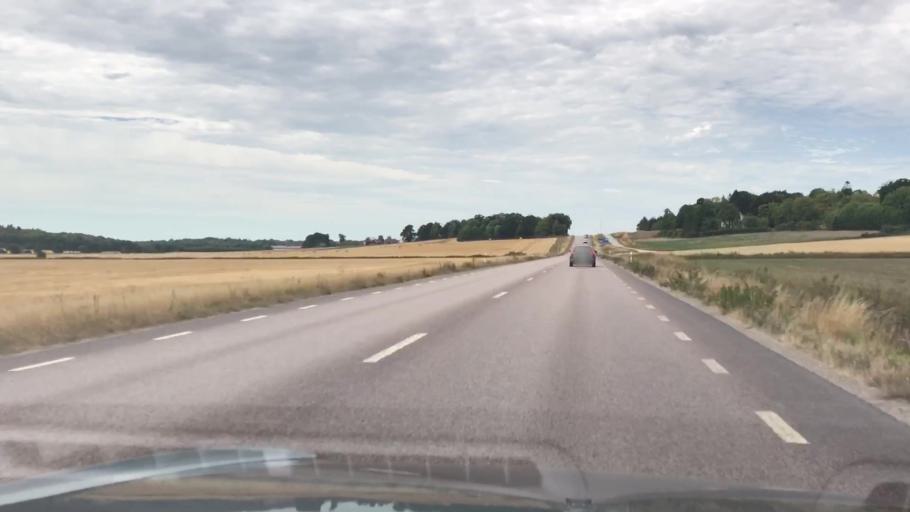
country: SE
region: Blekinge
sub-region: Karlskrona Kommun
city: Jaemjoe
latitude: 56.1864
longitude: 15.8055
